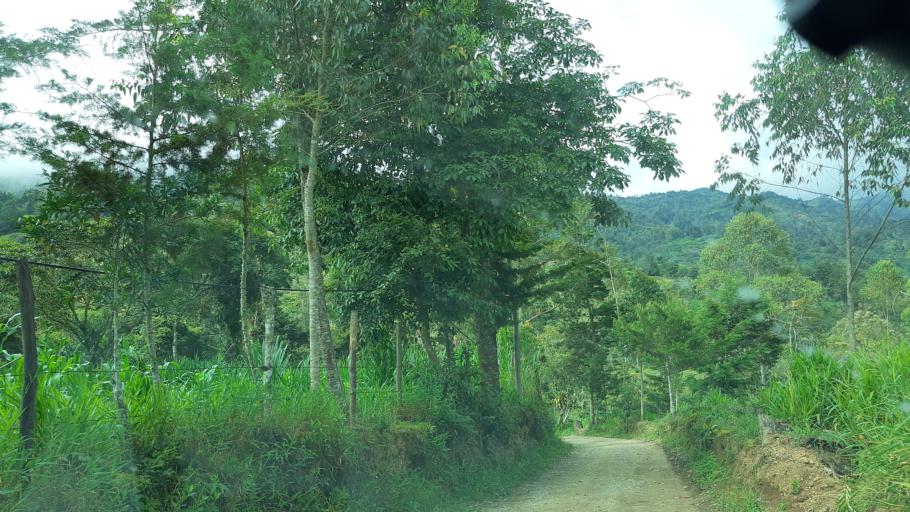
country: CO
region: Boyaca
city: Garagoa
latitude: 5.0403
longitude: -73.3454
